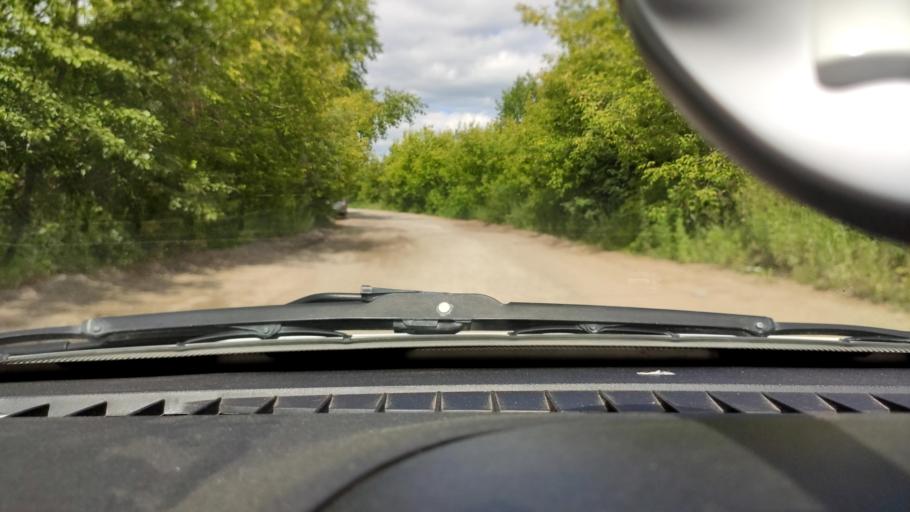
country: RU
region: Perm
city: Kondratovo
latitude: 58.0288
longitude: 56.0614
